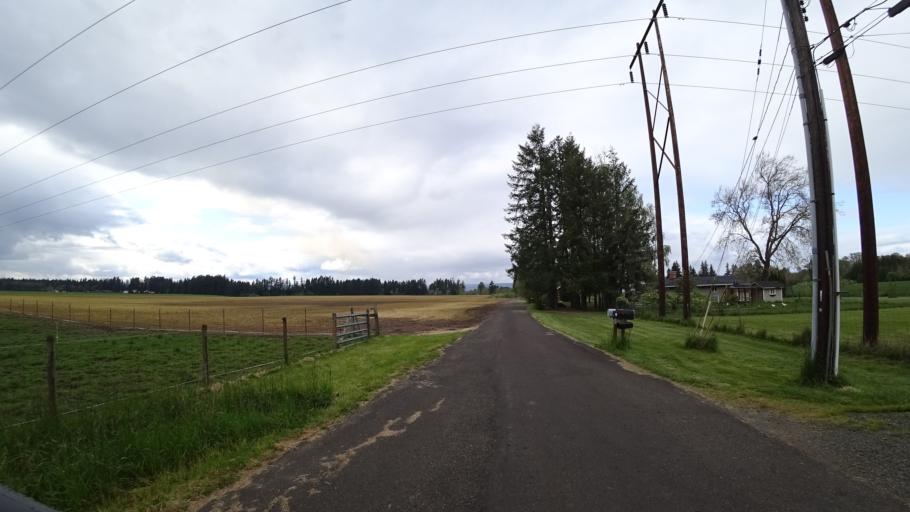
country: US
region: Oregon
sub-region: Washington County
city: Hillsboro
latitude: 45.5572
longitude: -122.9584
